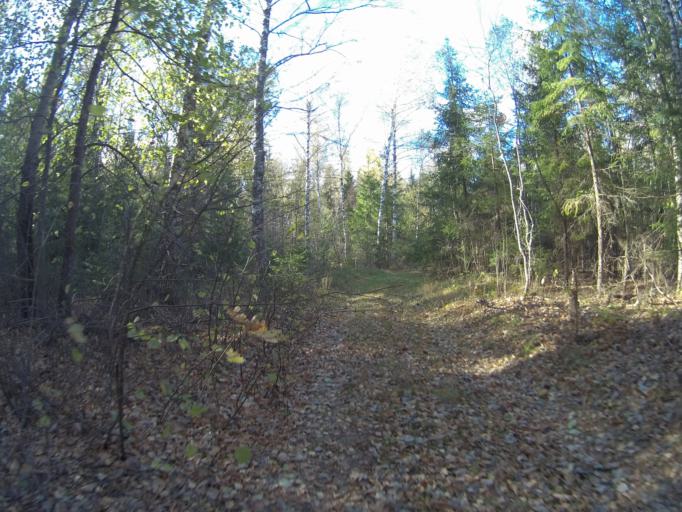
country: RU
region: Vladimir
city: Golovino
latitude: 55.9984
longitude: 40.4980
